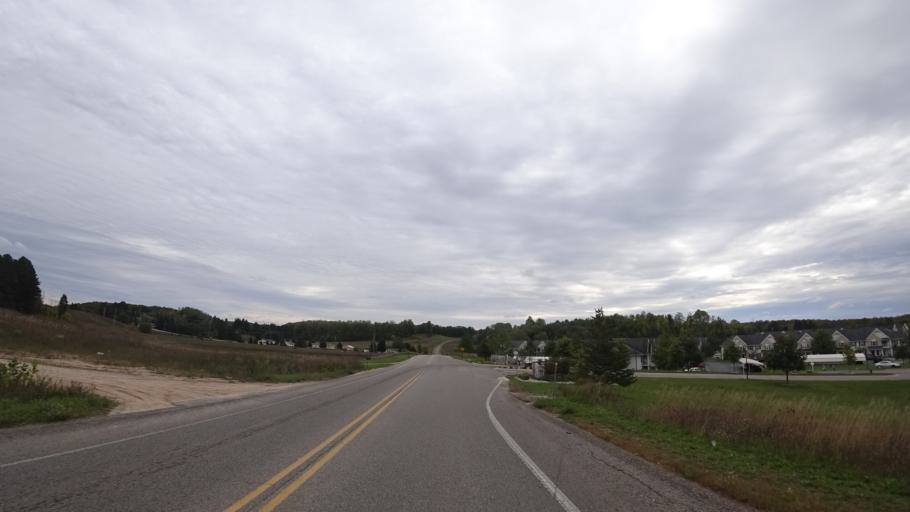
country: US
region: Michigan
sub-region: Emmet County
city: Petoskey
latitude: 45.3435
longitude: -84.9709
